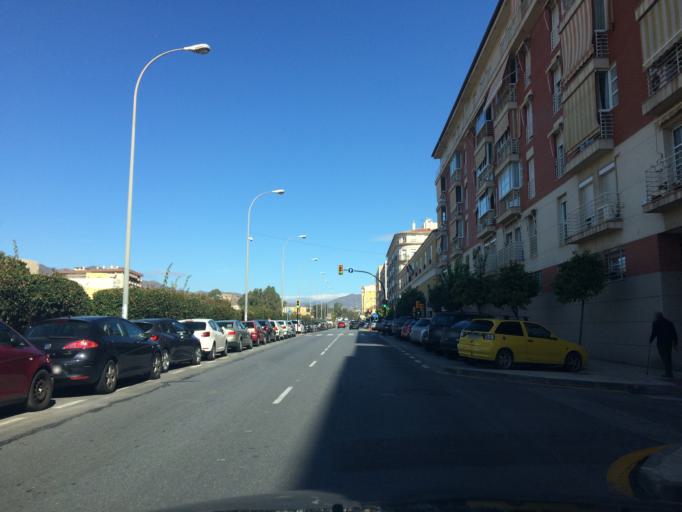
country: ES
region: Andalusia
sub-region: Provincia de Malaga
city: Malaga
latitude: 36.7240
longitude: -4.4255
